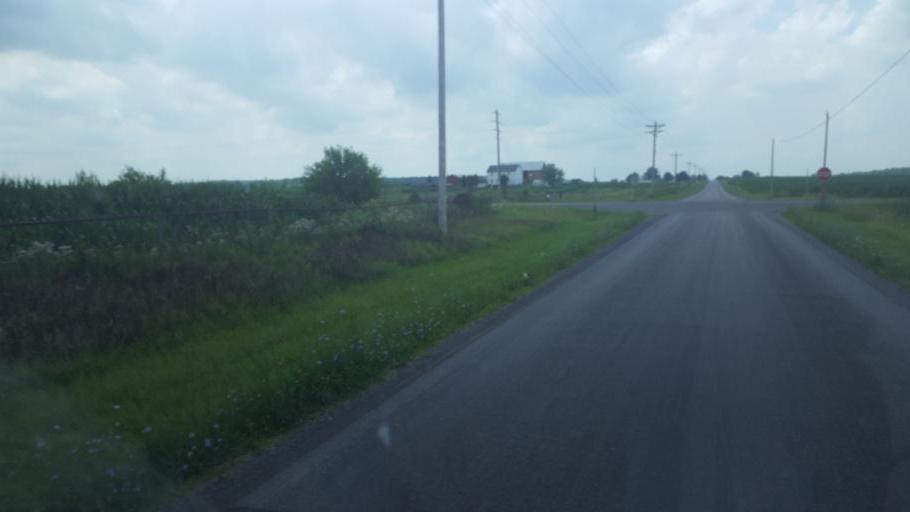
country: US
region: Ohio
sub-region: Hardin County
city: Kenton
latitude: 40.5776
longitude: -83.5903
